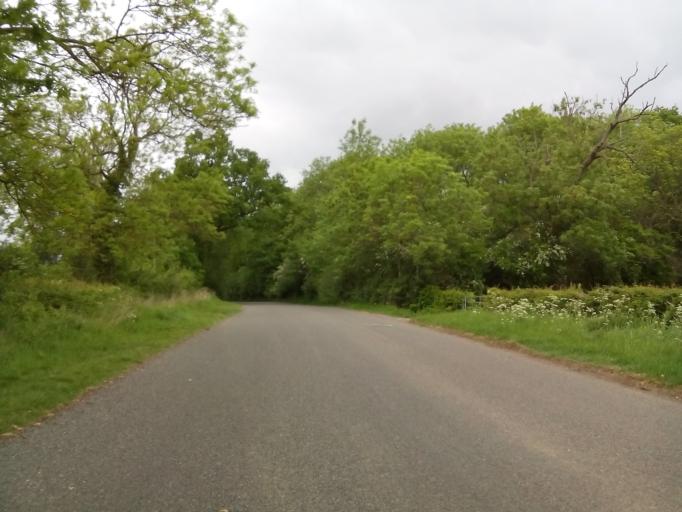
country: GB
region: England
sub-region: Northamptonshire
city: Oundle
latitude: 52.5103
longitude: -0.4929
